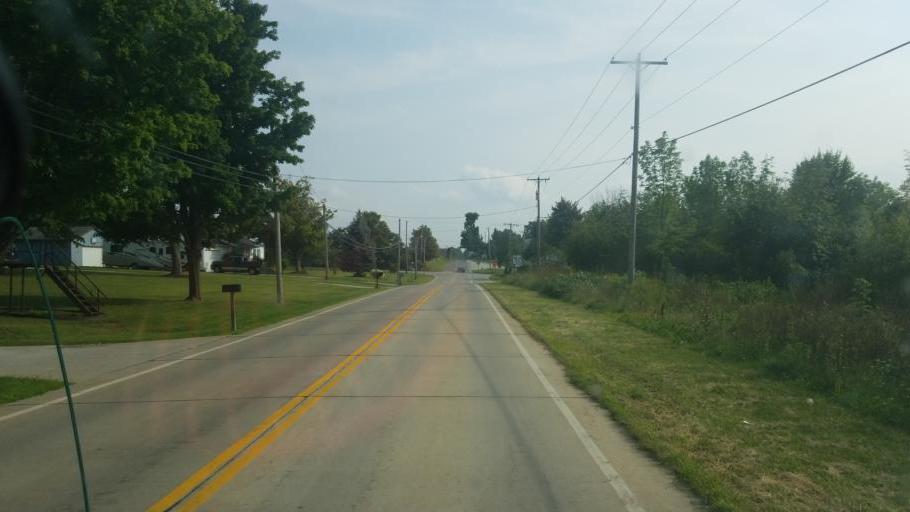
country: US
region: Ohio
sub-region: Medina County
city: Medina
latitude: 41.1009
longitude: -81.8840
